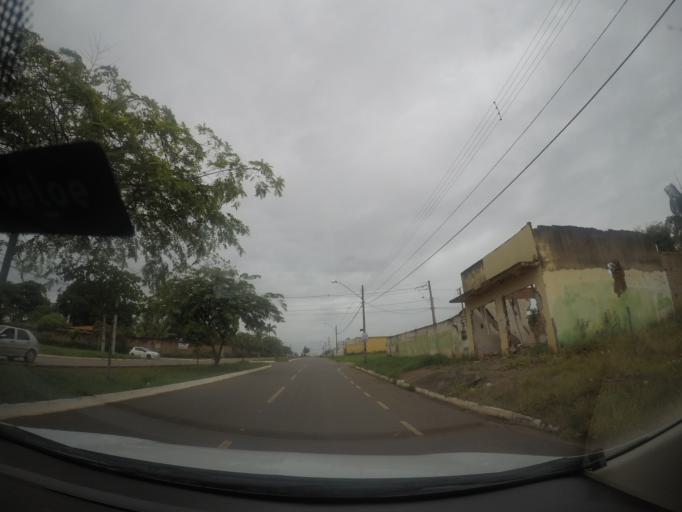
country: BR
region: Goias
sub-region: Goiania
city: Goiania
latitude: -16.6228
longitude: -49.3070
